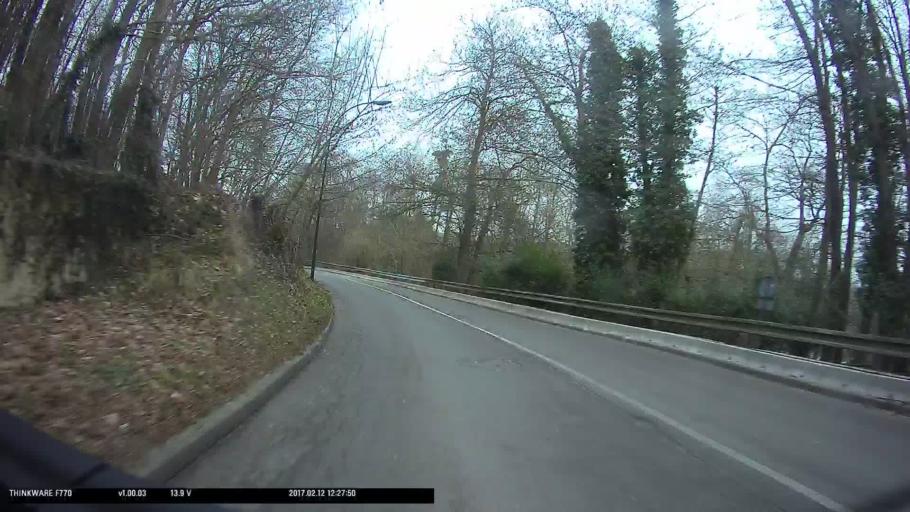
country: FR
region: Ile-de-France
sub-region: Departement du Val-d'Oise
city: Courdimanche
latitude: 49.0225
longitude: 2.0000
